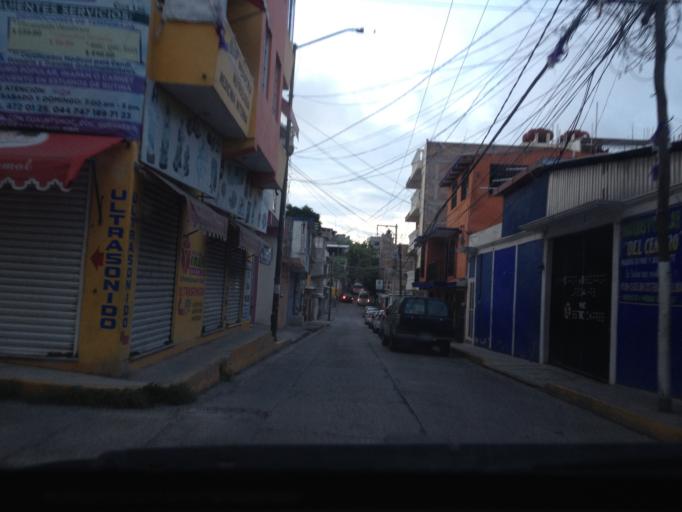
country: MX
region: Guerrero
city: Chilpancingo de los Bravos
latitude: 17.5594
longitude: -99.5022
